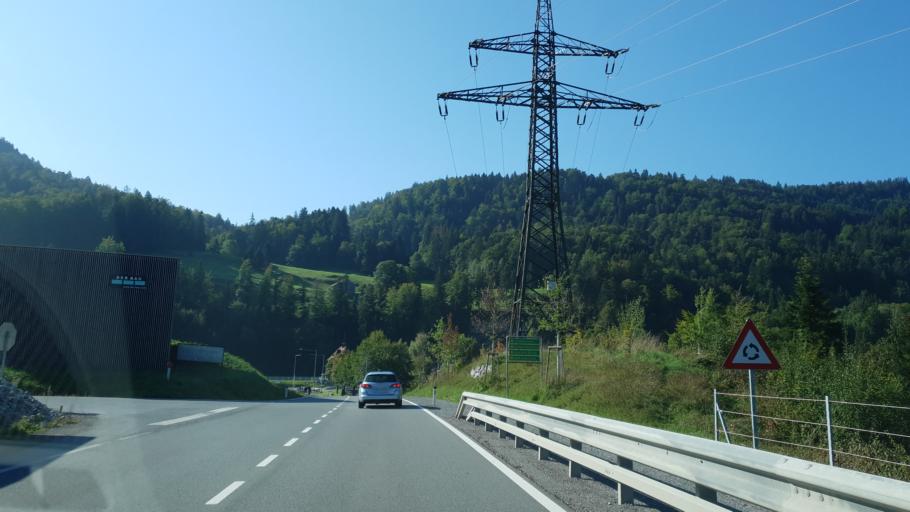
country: AT
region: Vorarlberg
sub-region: Politischer Bezirk Bregenz
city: Andelsbuch
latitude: 47.4040
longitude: 9.8788
